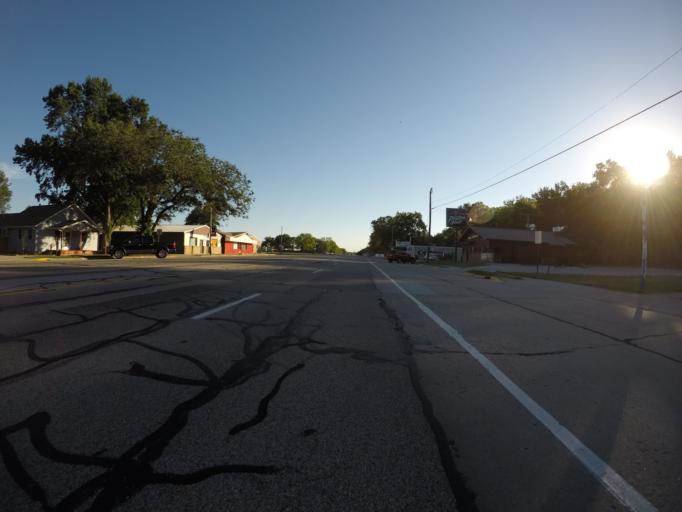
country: US
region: Kansas
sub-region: Riley County
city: Ogden
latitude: 39.1137
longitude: -96.7149
